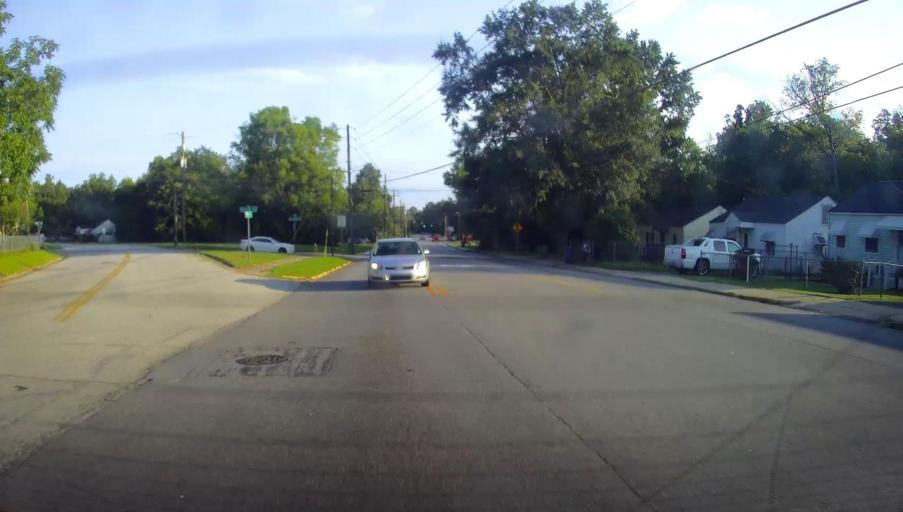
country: US
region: Georgia
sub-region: Bibb County
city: Macon
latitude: 32.8488
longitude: -83.6879
